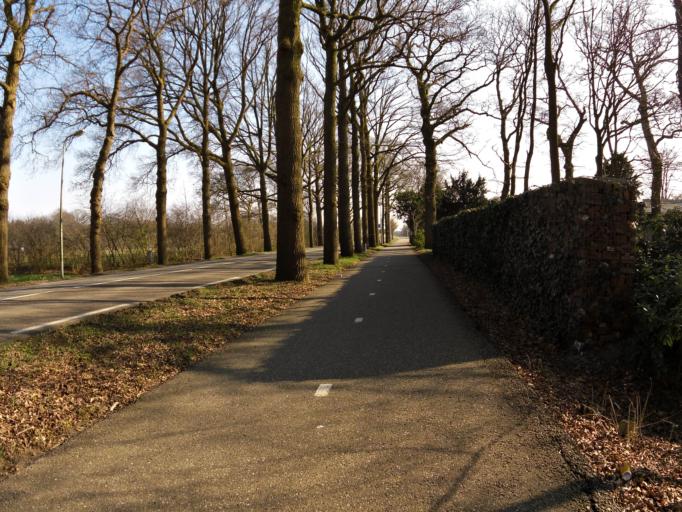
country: NL
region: North Brabant
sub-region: Gemeente Maasdonk
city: Geffen
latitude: 51.7172
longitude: 5.4016
